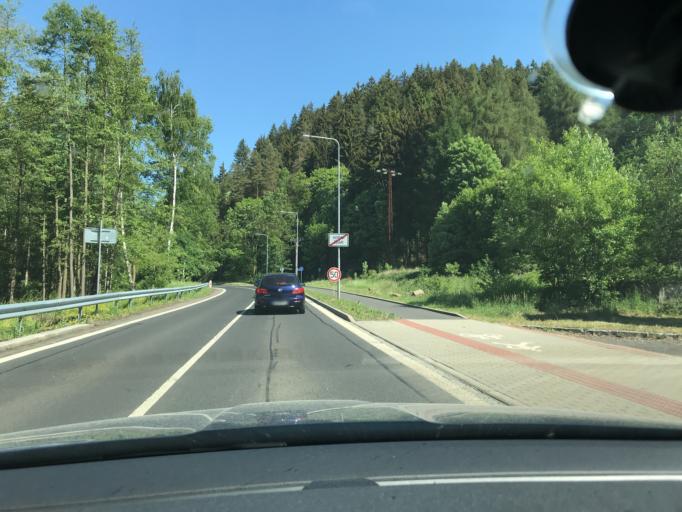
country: CZ
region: Karlovarsky
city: Jachymov
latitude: 50.3386
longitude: 12.9391
